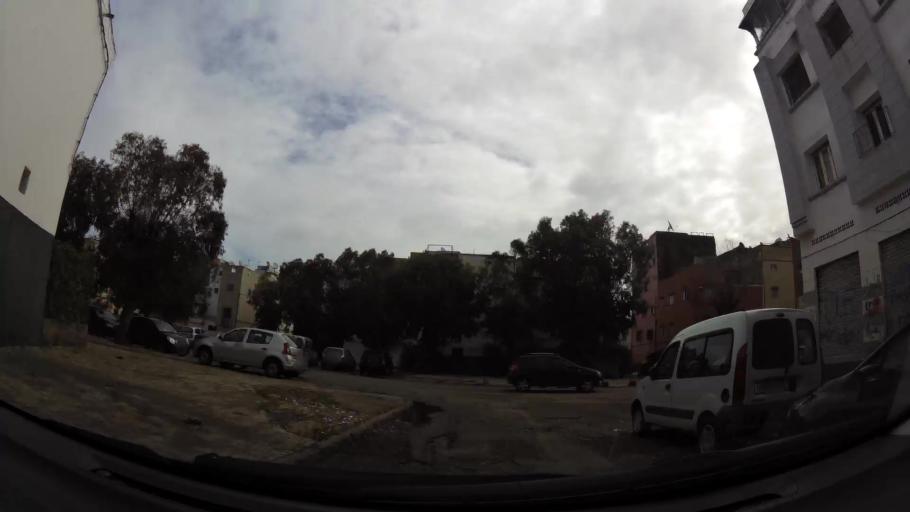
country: MA
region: Grand Casablanca
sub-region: Casablanca
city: Casablanca
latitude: 33.5715
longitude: -7.6705
